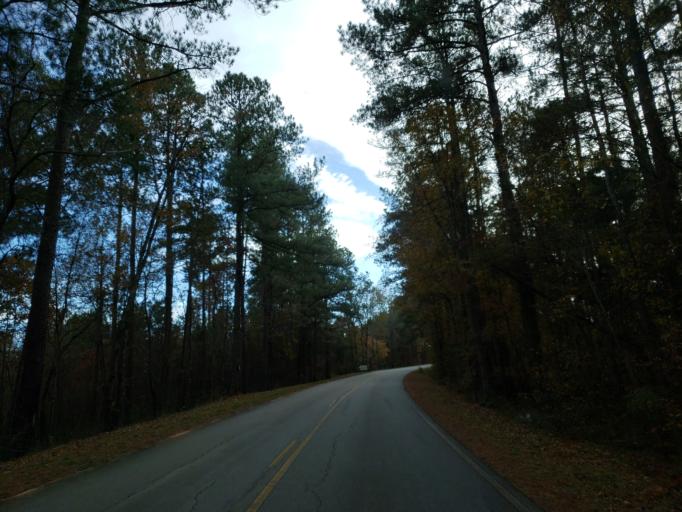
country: US
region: Georgia
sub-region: Monroe County
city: Forsyth
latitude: 33.0152
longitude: -83.8787
